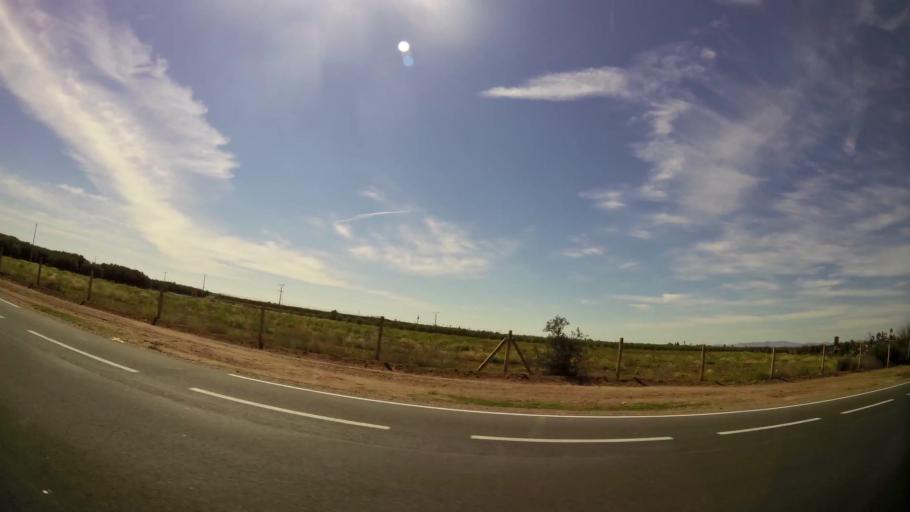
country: MA
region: Marrakech-Tensift-Al Haouz
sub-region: Marrakech
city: Marrakesh
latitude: 31.6536
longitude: -8.1053
